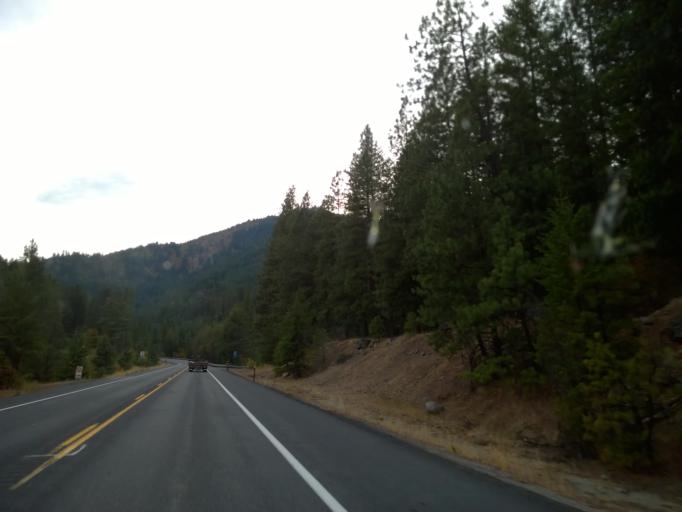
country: US
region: Washington
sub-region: Chelan County
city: Leavenworth
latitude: 47.4888
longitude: -120.6464
